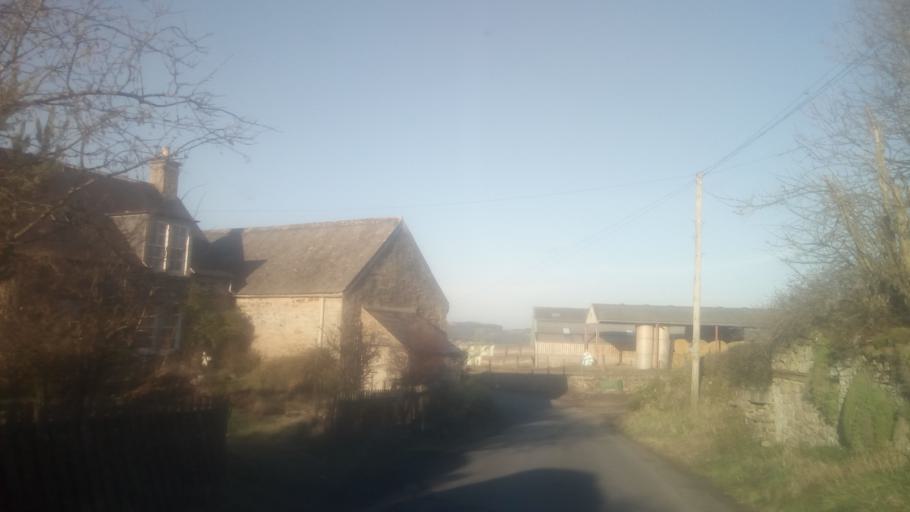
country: GB
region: Scotland
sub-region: The Scottish Borders
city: Jedburgh
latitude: 55.4896
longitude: -2.6015
